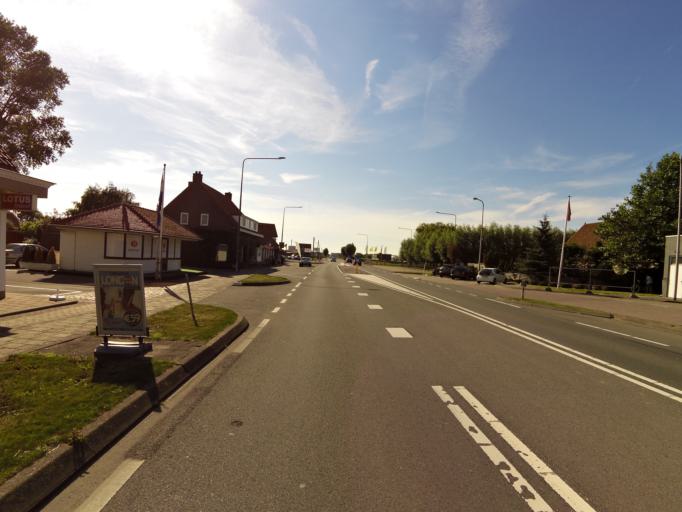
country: NL
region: Zeeland
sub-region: Gemeente Sluis
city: Sluis
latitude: 51.3144
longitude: 3.3604
